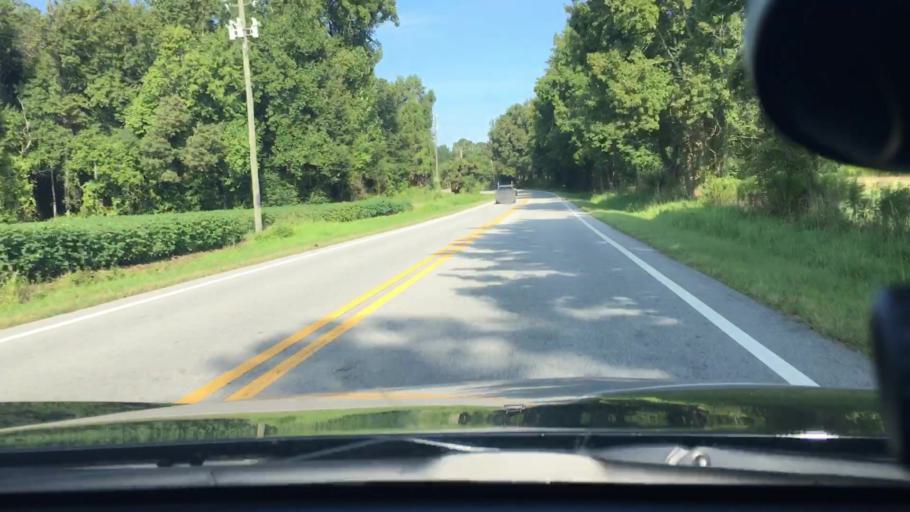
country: US
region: North Carolina
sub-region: Pitt County
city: Farmville
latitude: 35.6949
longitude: -77.5018
